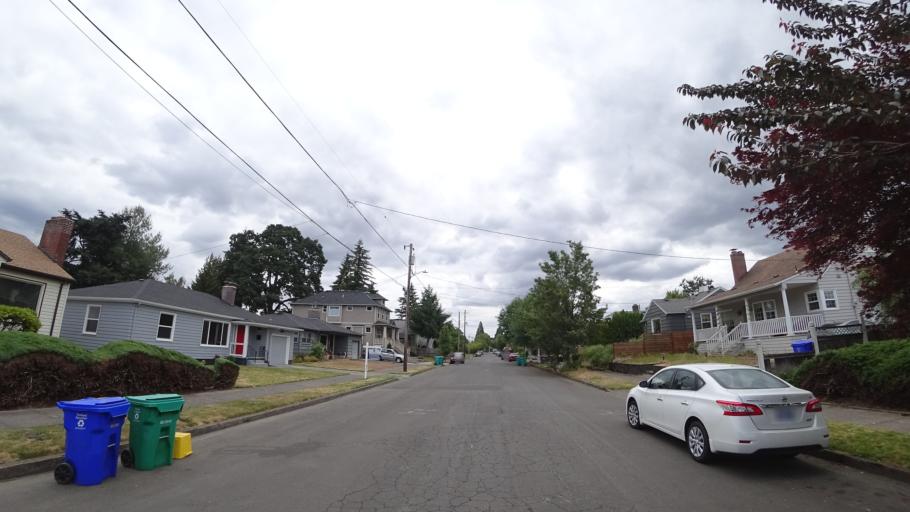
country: US
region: Oregon
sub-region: Multnomah County
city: Portland
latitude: 45.5759
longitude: -122.7233
